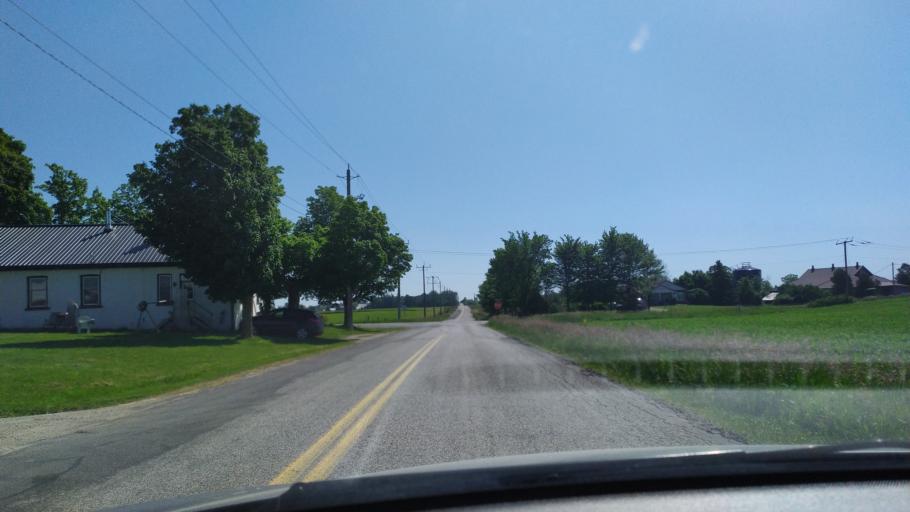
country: CA
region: Ontario
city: Waterloo
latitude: 43.4598
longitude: -80.7114
